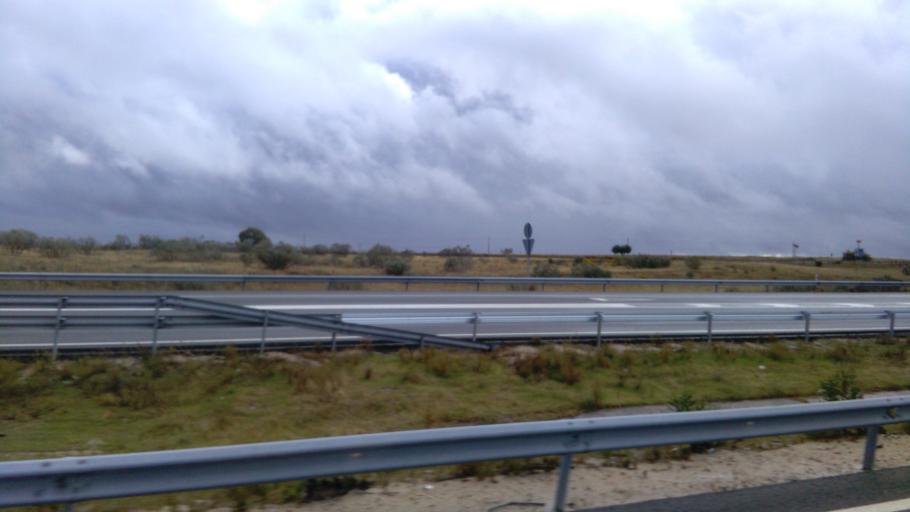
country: ES
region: Castille-La Mancha
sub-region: Province of Toledo
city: Valmojado
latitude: 40.1931
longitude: -4.1085
